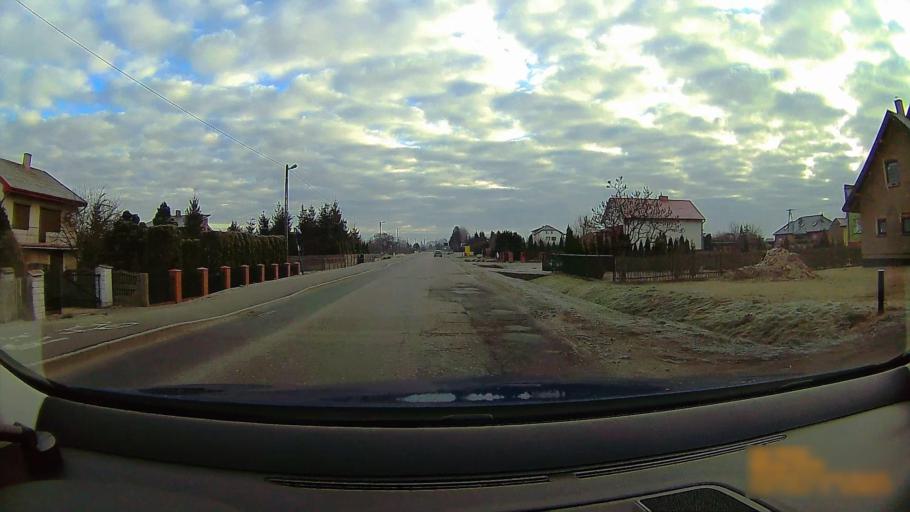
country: PL
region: Greater Poland Voivodeship
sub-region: Powiat koninski
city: Golina
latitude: 52.1986
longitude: 18.1425
